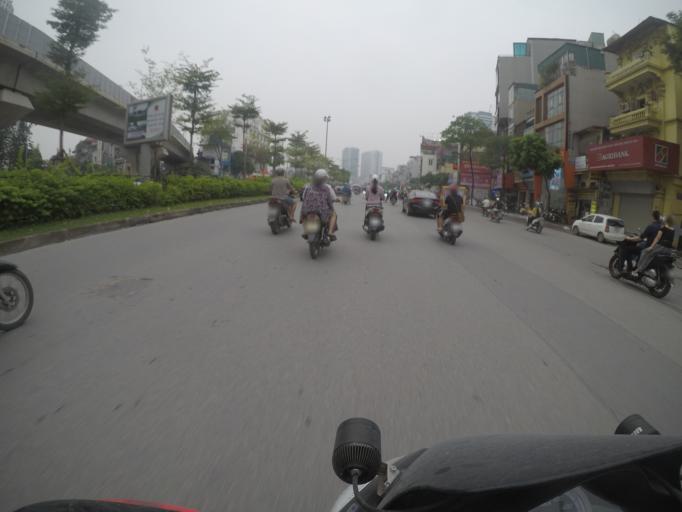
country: VN
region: Ha Noi
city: Thanh Xuan
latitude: 21.0009
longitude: 105.8172
